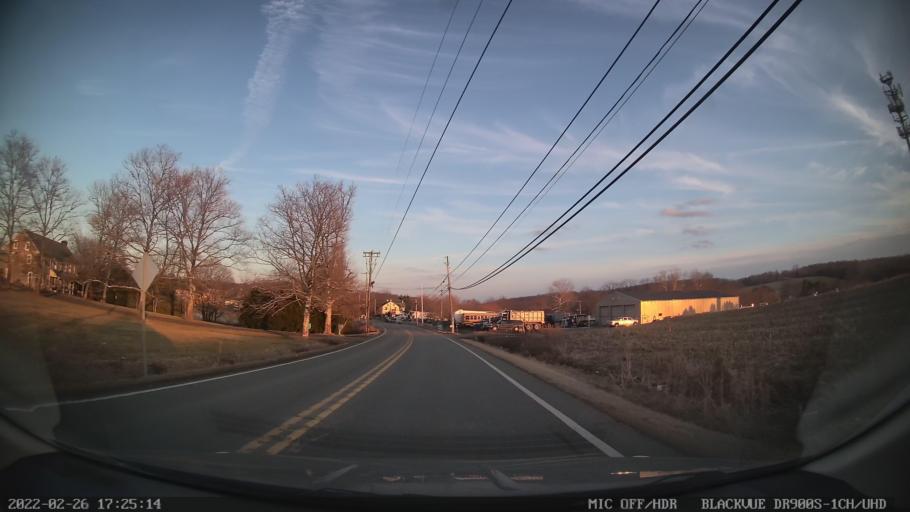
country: US
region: Pennsylvania
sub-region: Montgomery County
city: East Greenville
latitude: 40.4291
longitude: -75.5401
